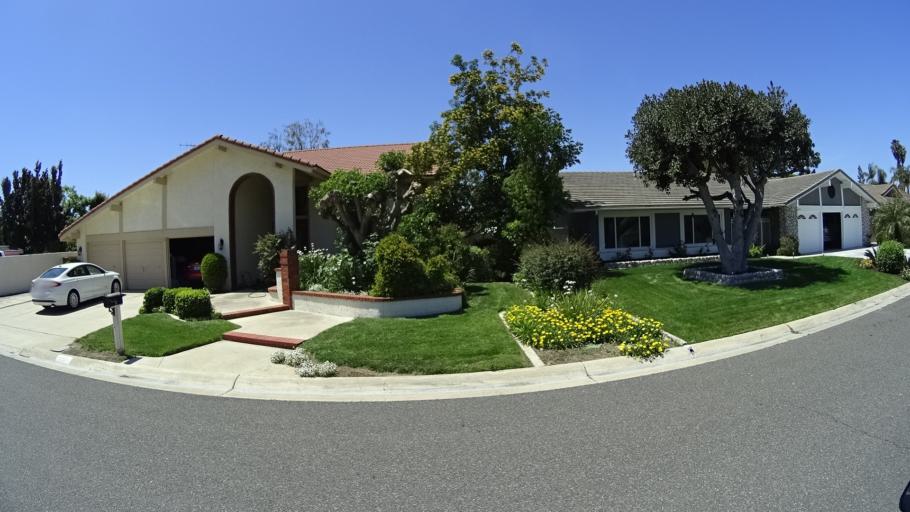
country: US
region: California
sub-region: Orange County
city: Villa Park
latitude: 33.8085
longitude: -117.8192
